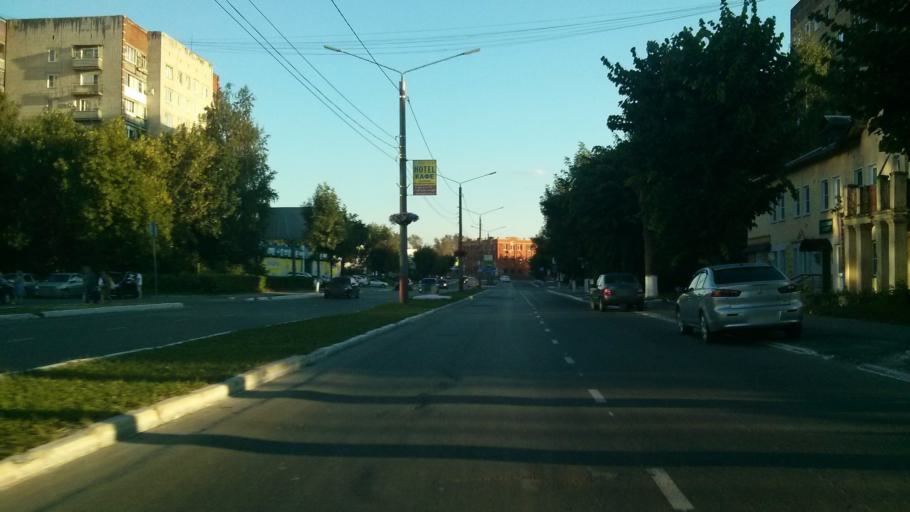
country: RU
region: Vladimir
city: Murom
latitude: 55.5774
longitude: 42.0355
